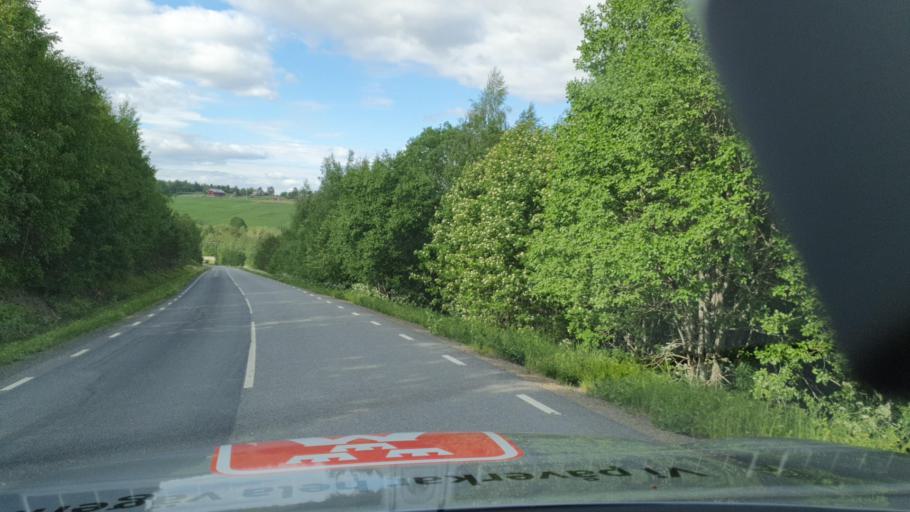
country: SE
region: Vaesternorrland
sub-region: Kramfors Kommun
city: Nordingra
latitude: 62.8373
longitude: 18.2015
